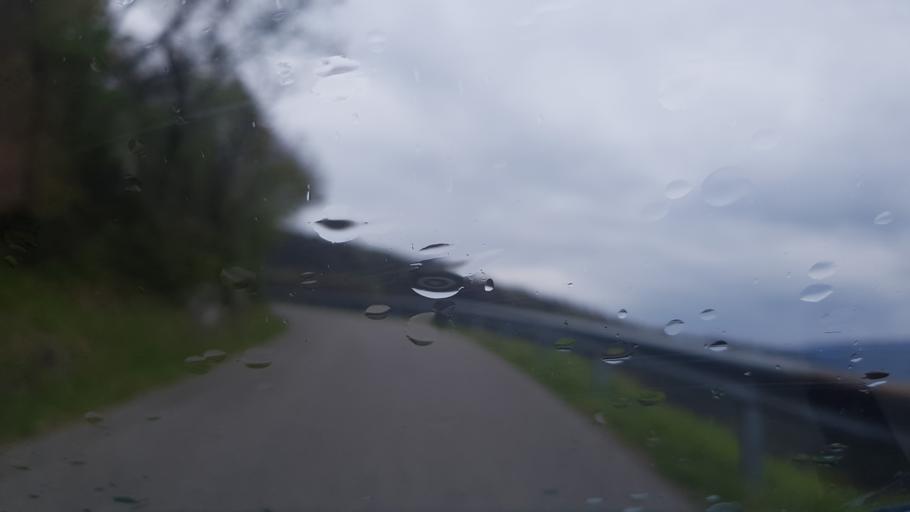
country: SI
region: Kanal
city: Deskle
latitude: 46.0401
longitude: 13.5671
